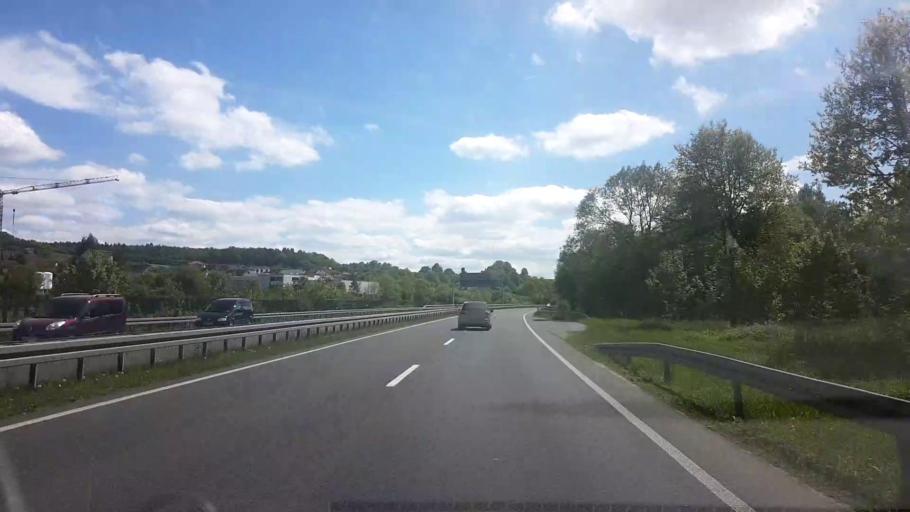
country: DE
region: Bavaria
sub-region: Upper Franconia
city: Niederfullbach
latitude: 50.2173
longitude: 10.9830
